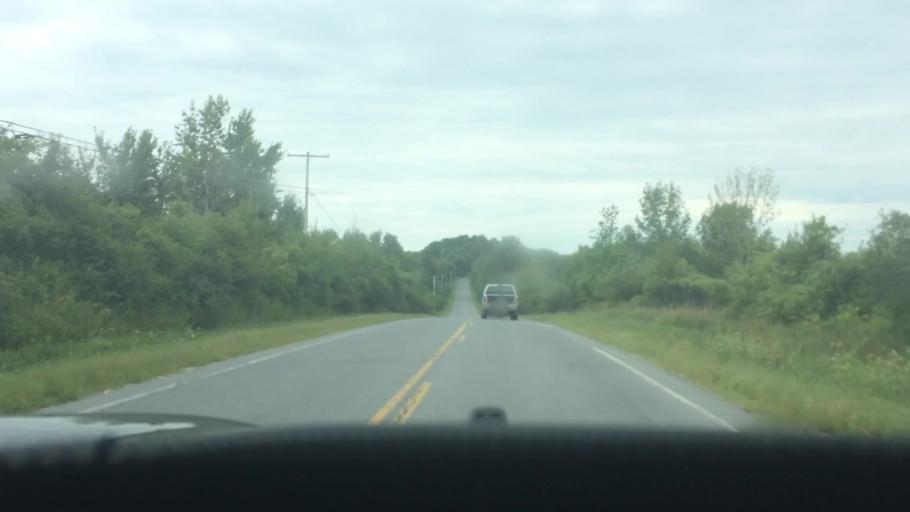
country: US
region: New York
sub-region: St. Lawrence County
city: Canton
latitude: 44.4830
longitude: -75.2222
